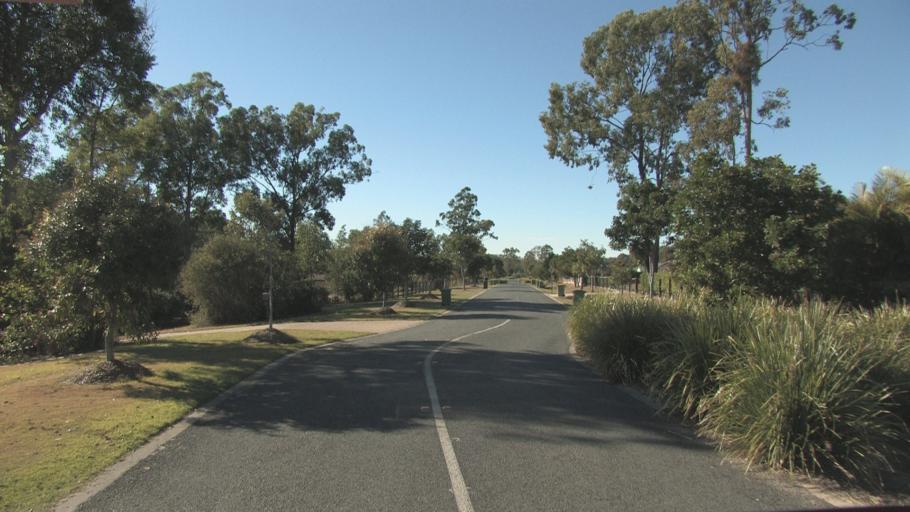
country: AU
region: Queensland
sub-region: Logan
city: North Maclean
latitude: -27.7476
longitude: 152.9618
